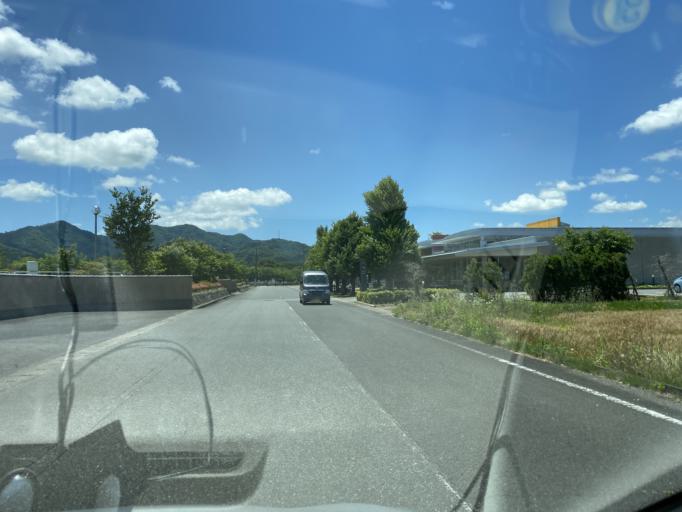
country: JP
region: Hyogo
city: Toyooka
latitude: 35.4874
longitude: 134.8070
